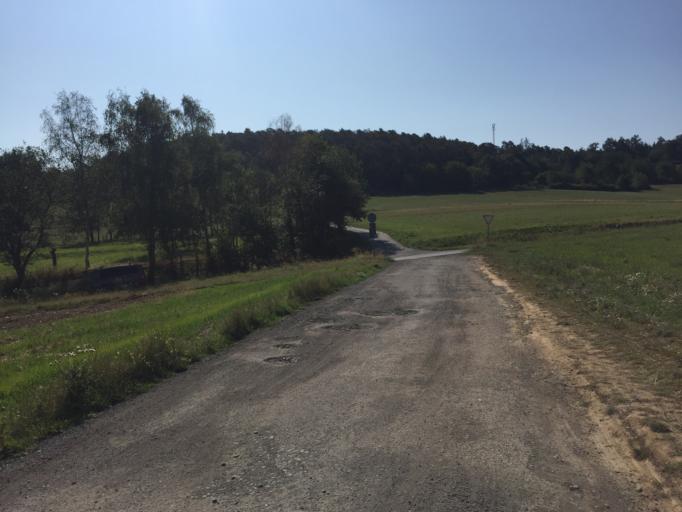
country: DE
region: Hesse
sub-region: Regierungsbezirk Giessen
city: Schoeffengrund
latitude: 50.4412
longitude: 8.5602
